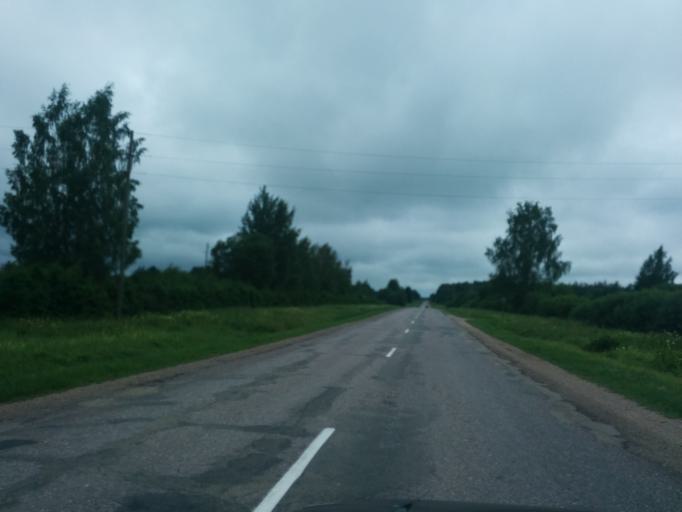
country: LV
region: Balvu Rajons
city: Balvi
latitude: 57.1480
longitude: 27.2313
